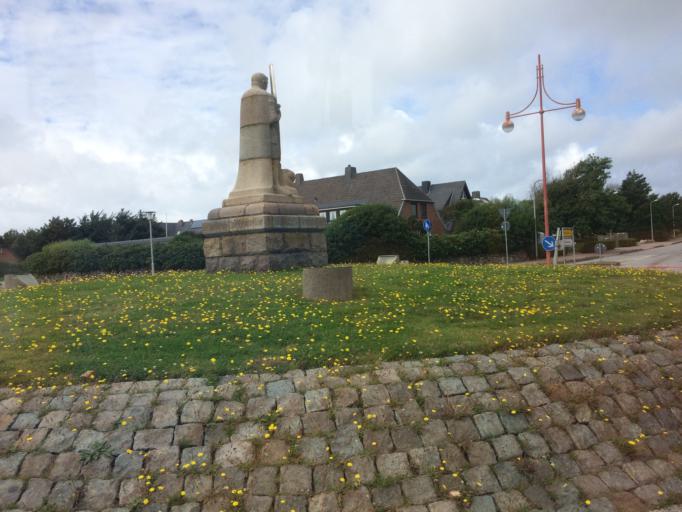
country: DE
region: Schleswig-Holstein
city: Westerland
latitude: 54.9181
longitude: 8.3086
